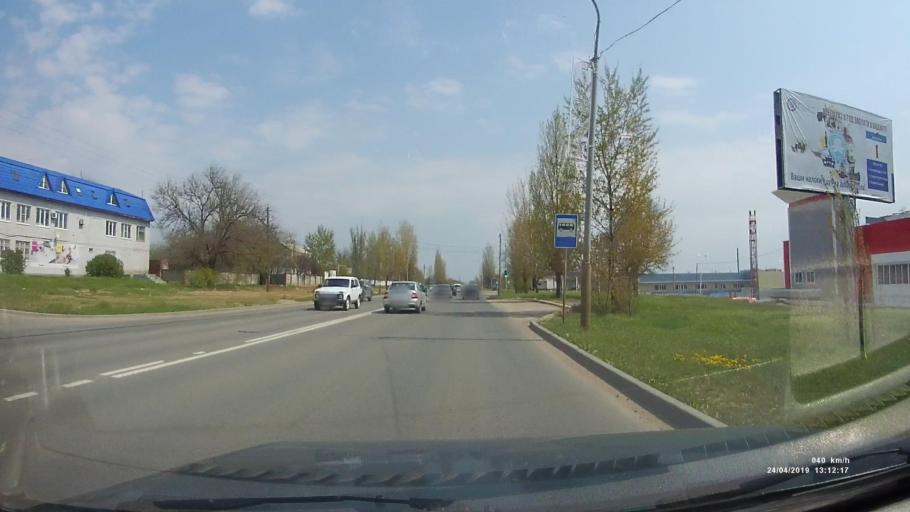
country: RU
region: Kalmykiya
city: Elista
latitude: 46.3131
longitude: 44.3024
